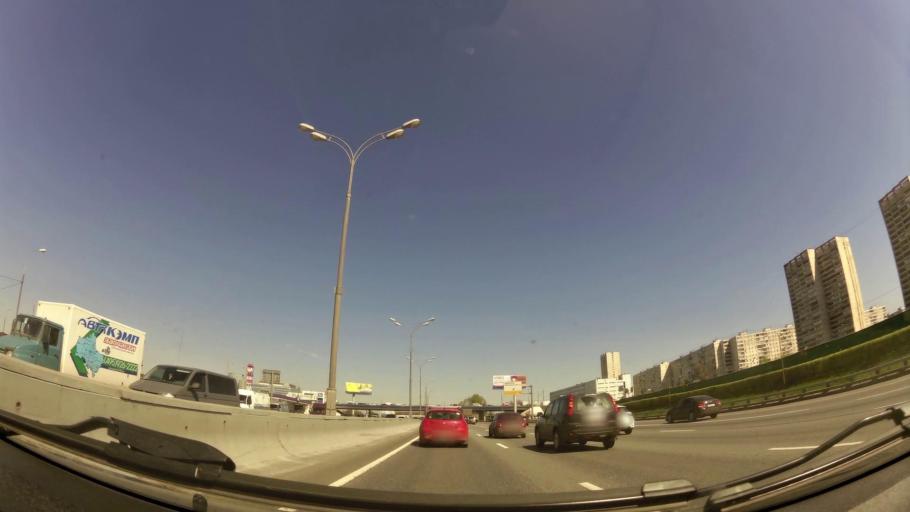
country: RU
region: Moscow
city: Strogino
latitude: 55.8071
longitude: 37.3878
